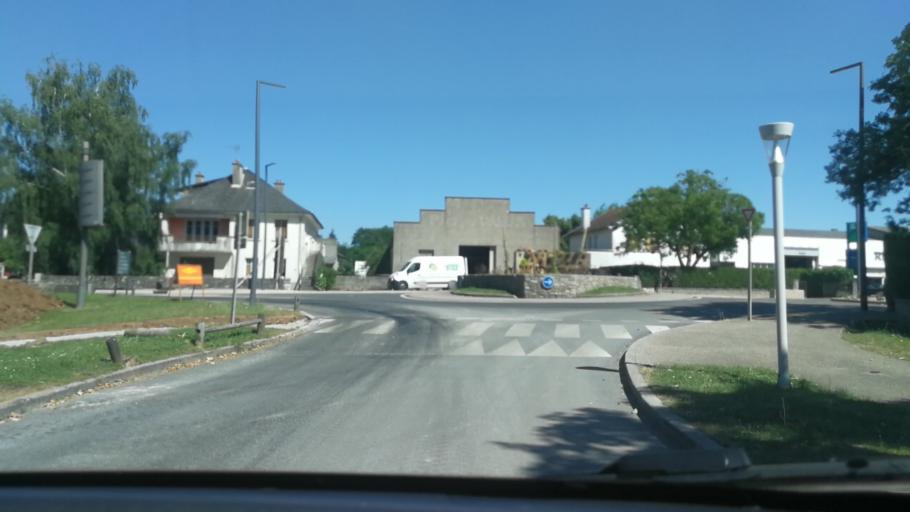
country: FR
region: Midi-Pyrenees
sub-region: Departement de l'Aveyron
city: Sebazac-Concoures
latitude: 44.3988
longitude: 2.5979
